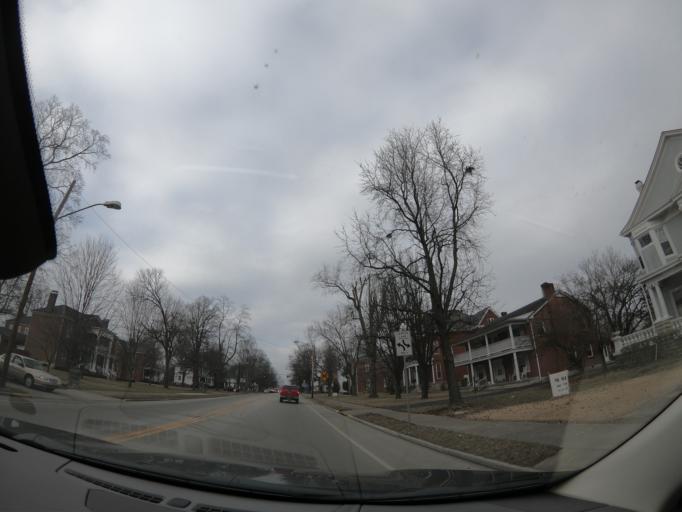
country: US
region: Kentucky
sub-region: Nelson County
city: Bardstown
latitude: 37.8140
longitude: -85.4653
